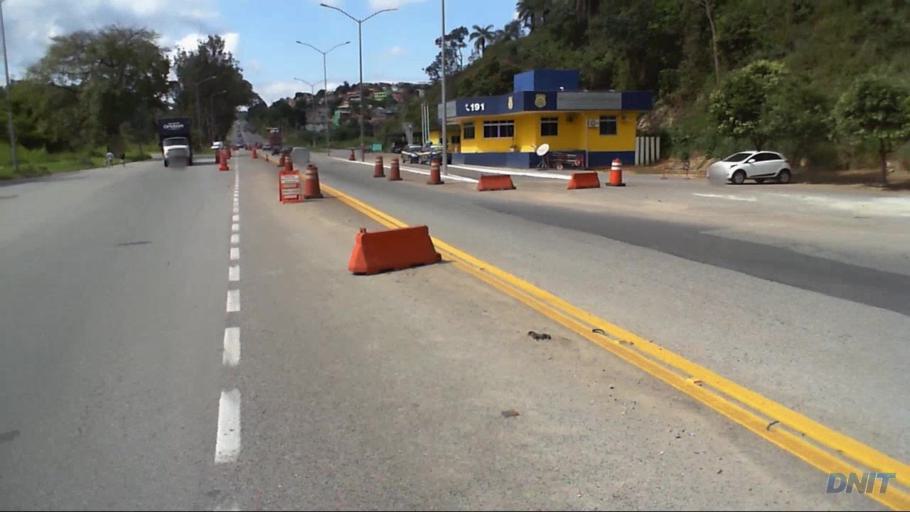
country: BR
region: Minas Gerais
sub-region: Santa Luzia
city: Santa Luzia
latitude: -19.8277
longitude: -43.8387
